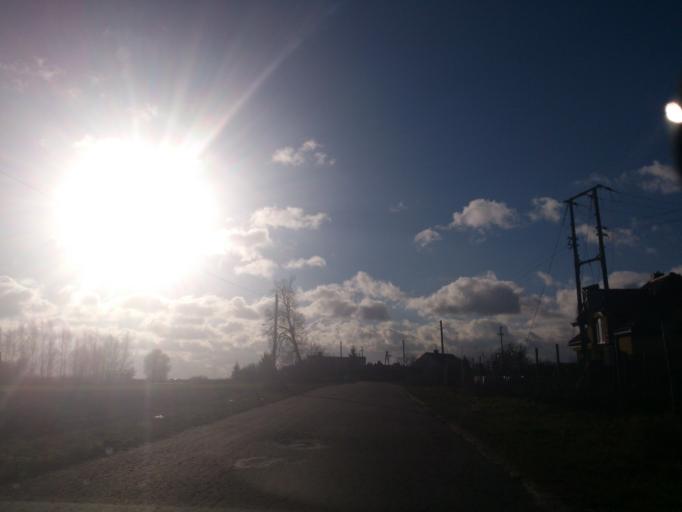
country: PL
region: Kujawsko-Pomorskie
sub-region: Powiat torunski
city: Lubicz Gorny
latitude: 53.0421
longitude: 18.8151
